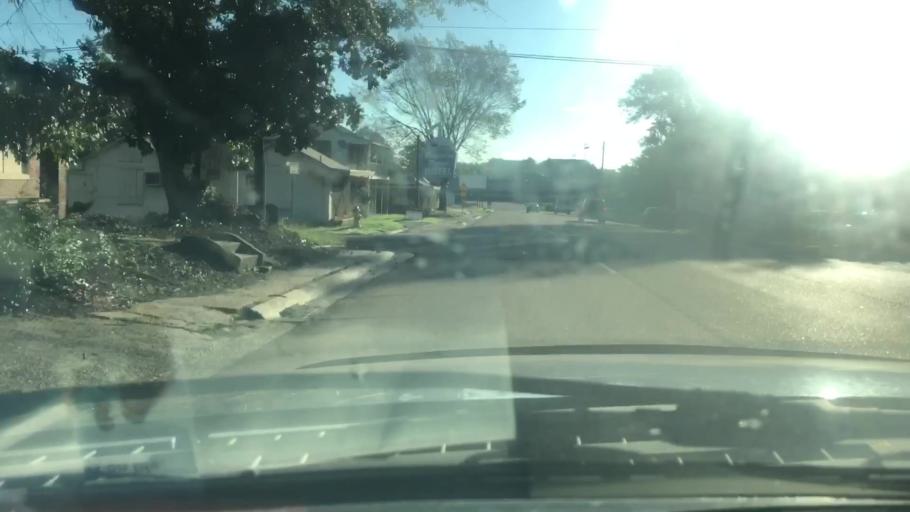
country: US
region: Texas
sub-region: Bowie County
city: Texarkana
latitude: 33.4233
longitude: -94.0555
